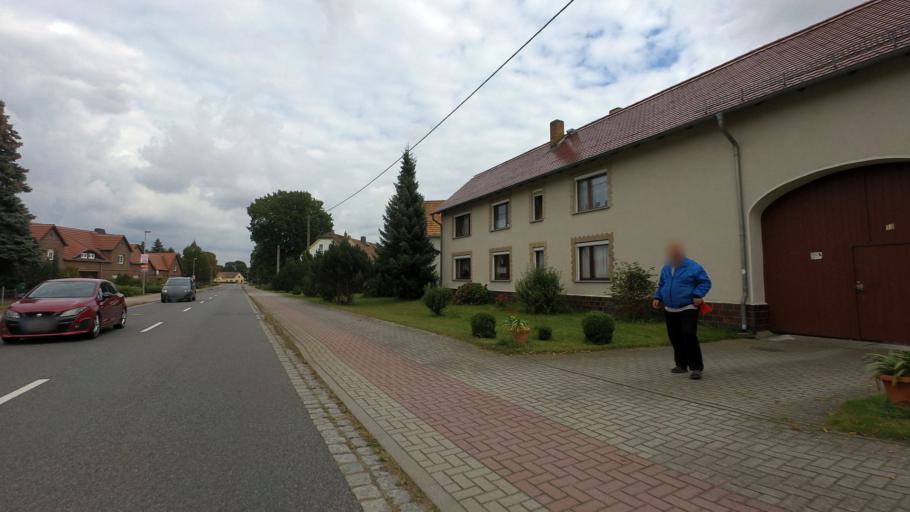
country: DE
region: Saxony
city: Hoyerswerda
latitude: 51.4558
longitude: 14.1970
